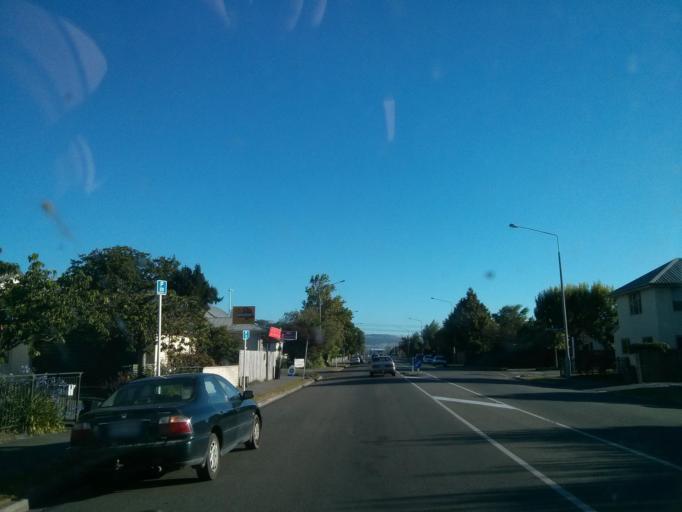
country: NZ
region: Canterbury
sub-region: Christchurch City
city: Christchurch
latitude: -43.5350
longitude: 172.5962
